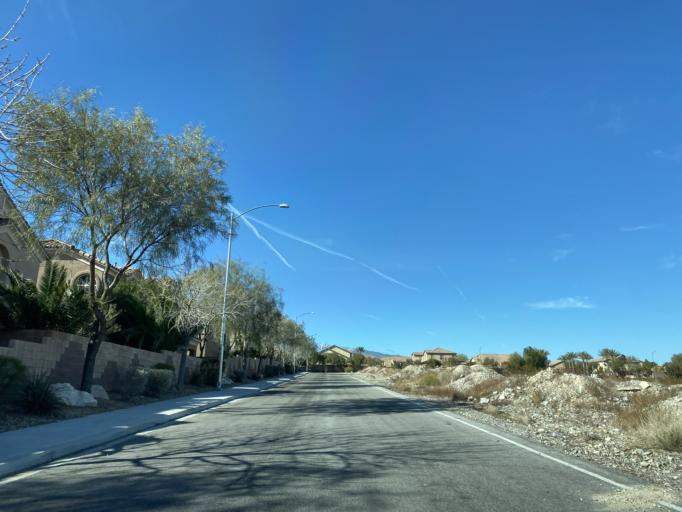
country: US
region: Nevada
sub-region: Clark County
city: Summerlin South
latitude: 36.3011
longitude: -115.3041
